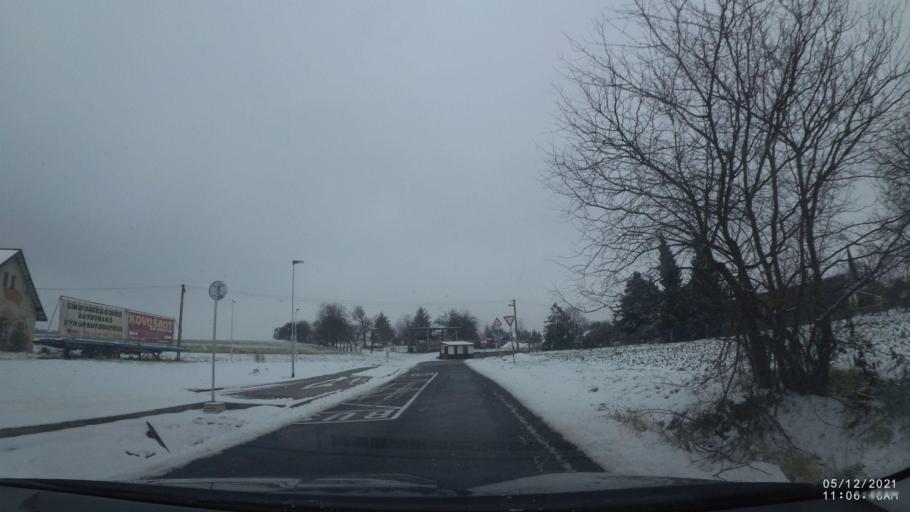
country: CZ
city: Solnice
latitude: 50.1814
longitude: 16.2219
